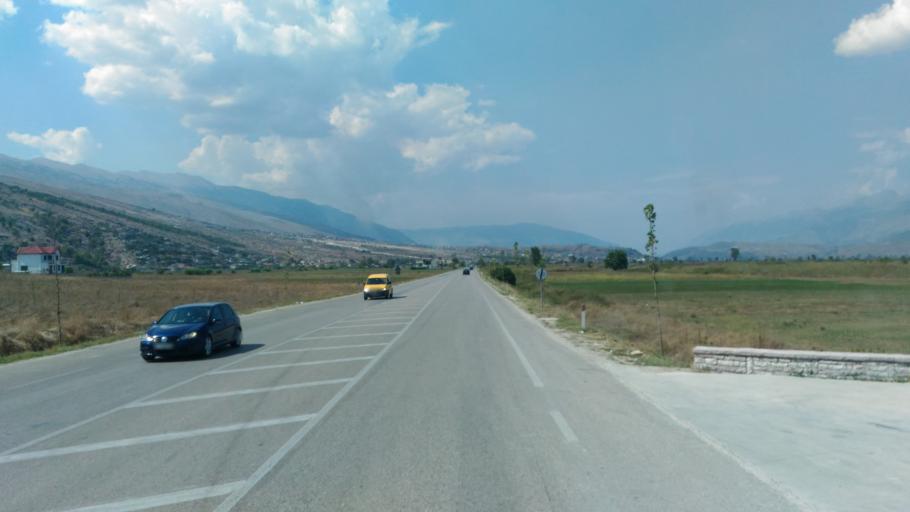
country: AL
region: Gjirokaster
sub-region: Rrethi i Gjirokastres
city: Dervician
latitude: 40.0217
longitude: 20.1932
